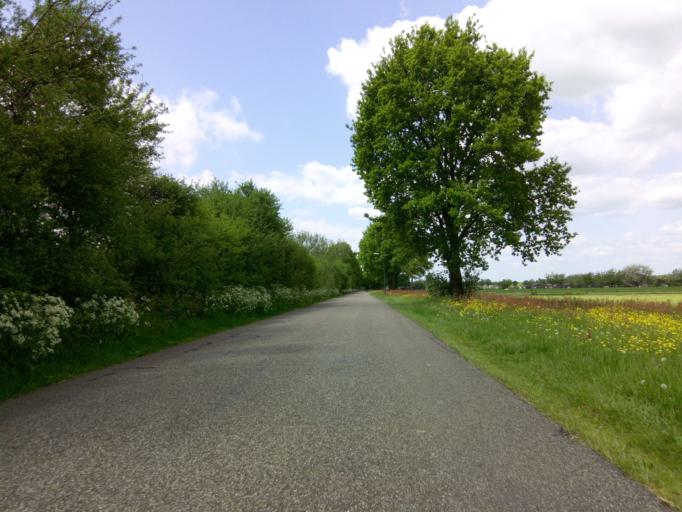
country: NL
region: Utrecht
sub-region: Gemeente Utrechtse Heuvelrug
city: Overberg
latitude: 52.0509
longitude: 5.5058
